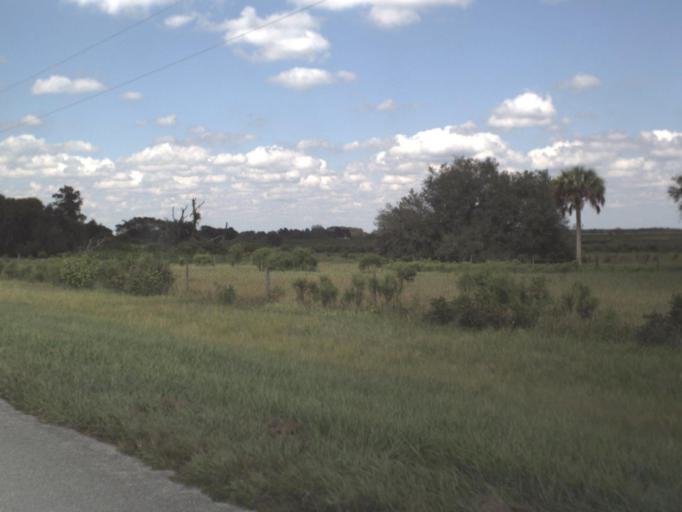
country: US
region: Florida
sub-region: Highlands County
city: Lake Placid
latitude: 27.3798
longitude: -81.1049
